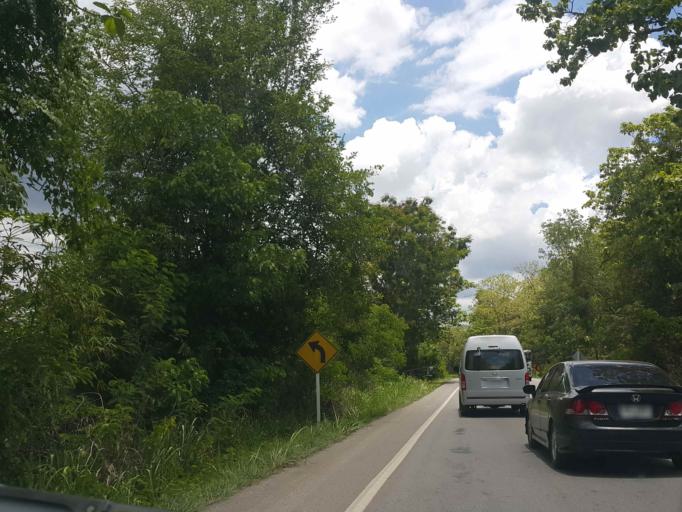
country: TH
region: Nan
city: Wiang Sa
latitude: 18.5192
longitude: 100.5866
